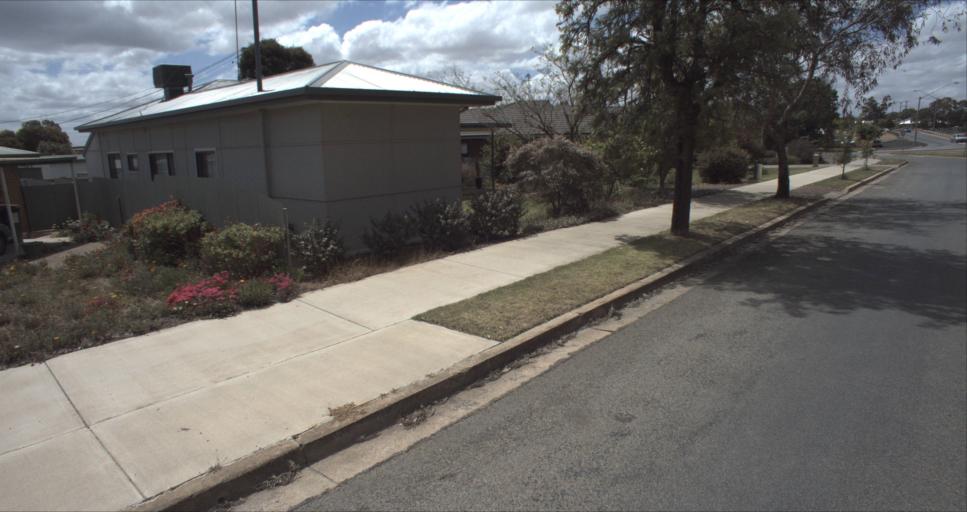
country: AU
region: New South Wales
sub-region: Leeton
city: Leeton
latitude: -34.5574
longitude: 146.3990
